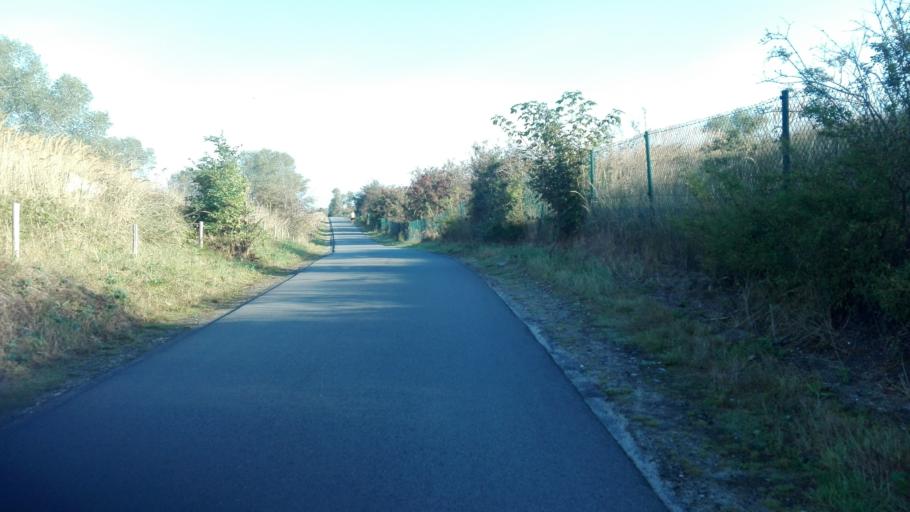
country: FR
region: Nord-Pas-de-Calais
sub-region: Departement du Nord
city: Ghyvelde
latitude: 51.0601
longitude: 2.5627
